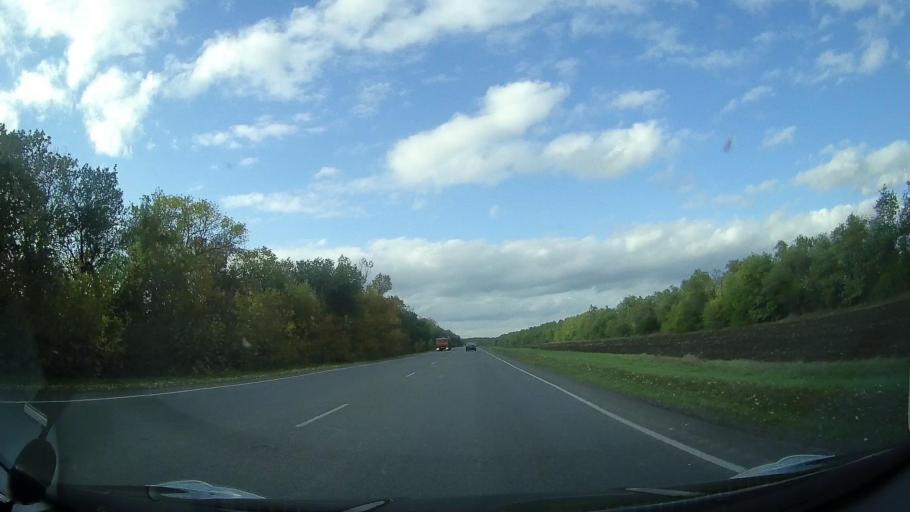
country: RU
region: Rostov
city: Kirovskaya
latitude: 46.9519
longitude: 40.0805
